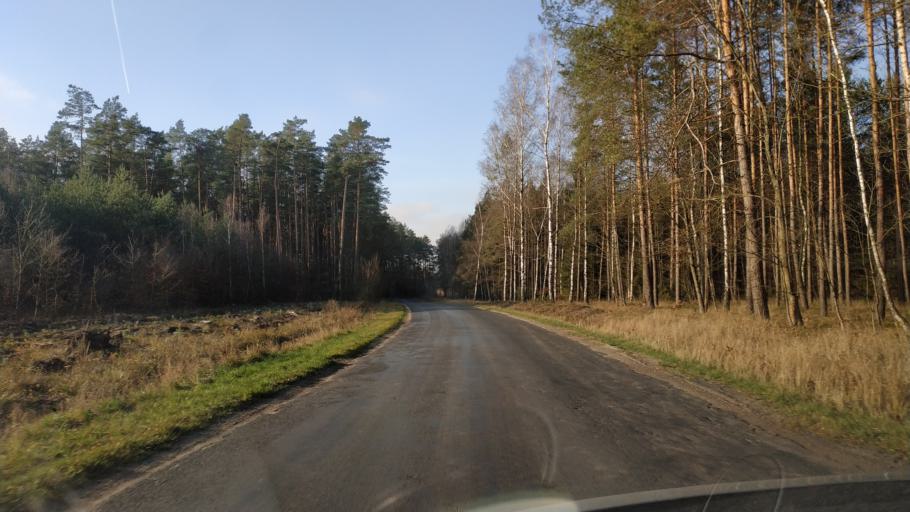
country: PL
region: Warmian-Masurian Voivodeship
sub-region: Powiat nowomiejski
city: Biskupiec
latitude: 53.4492
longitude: 19.4167
